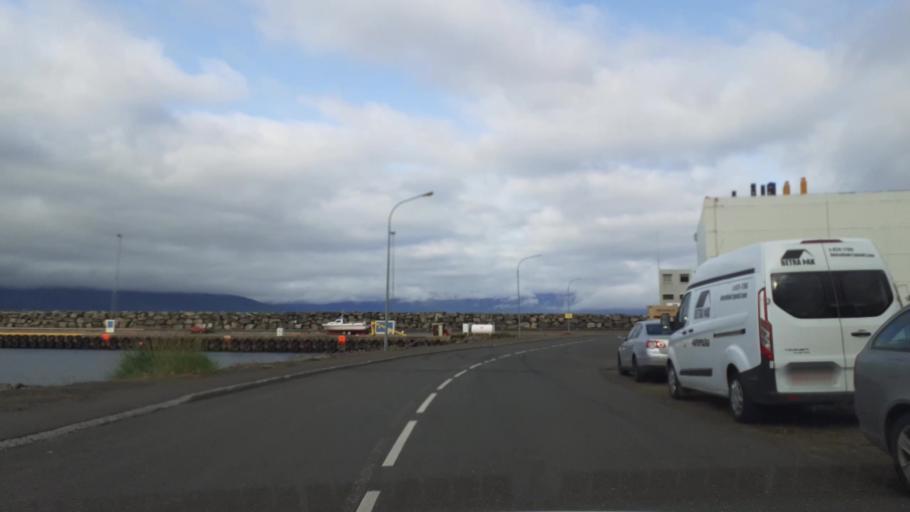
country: IS
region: Northeast
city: Akureyri
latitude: 65.9539
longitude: -18.1832
